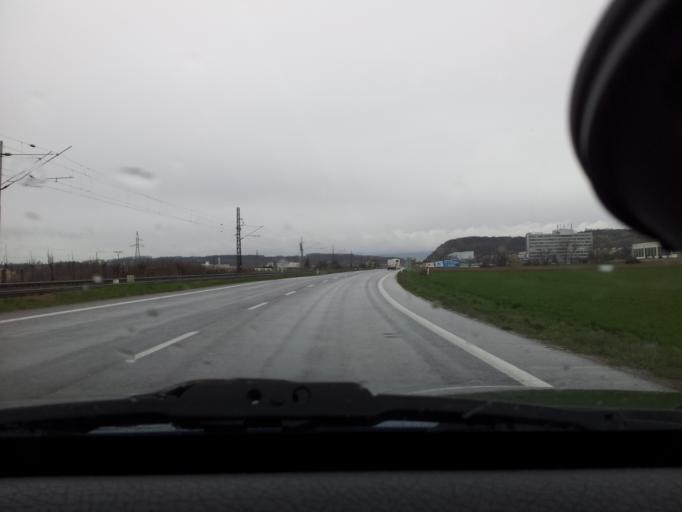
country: SK
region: Nitriansky
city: Tlmace
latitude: 48.2846
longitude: 18.5452
